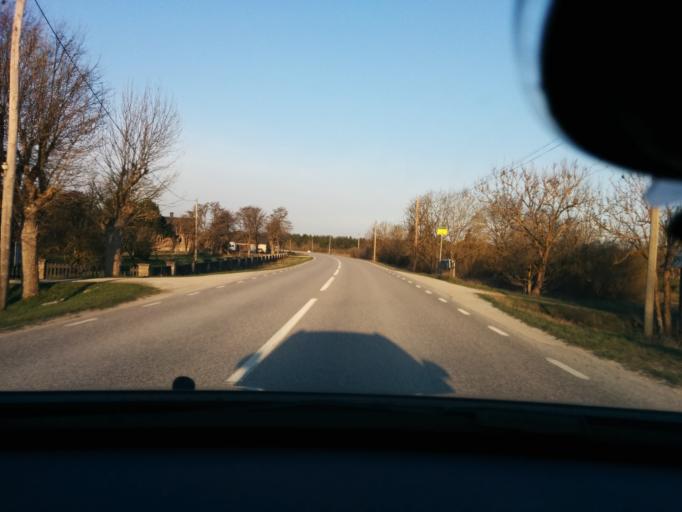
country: SE
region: Gotland
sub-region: Gotland
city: Visby
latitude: 57.6379
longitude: 18.4643
